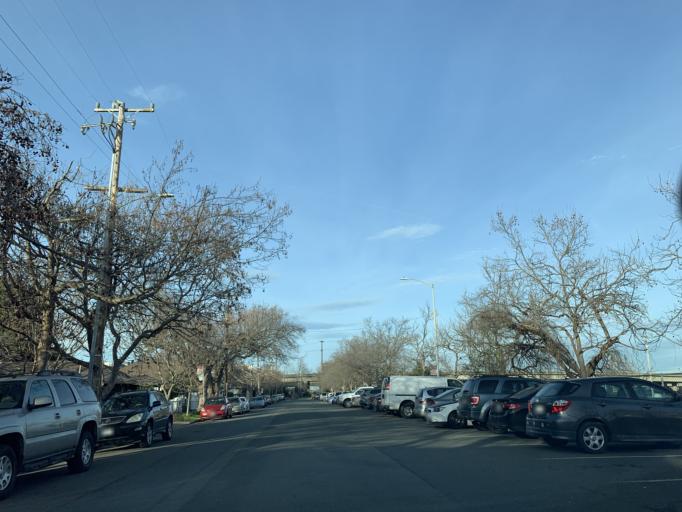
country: US
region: California
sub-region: Contra Costa County
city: North Richmond
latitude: 37.9259
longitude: -122.3843
